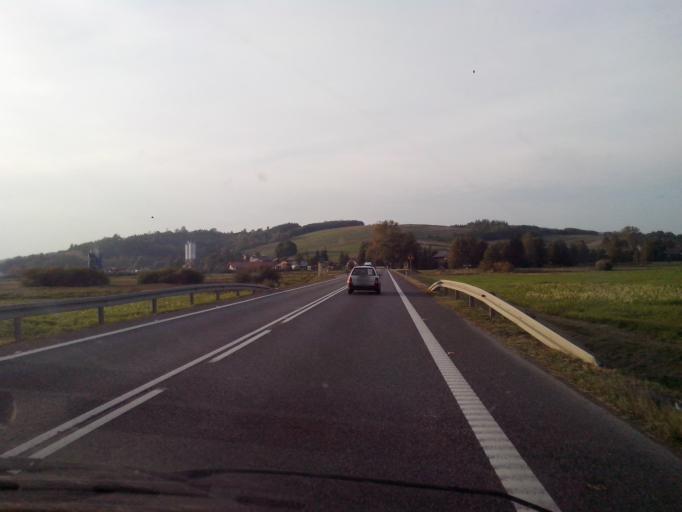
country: PL
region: Subcarpathian Voivodeship
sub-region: Powiat brzozowski
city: Domaradz
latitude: 49.8006
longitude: 21.9297
